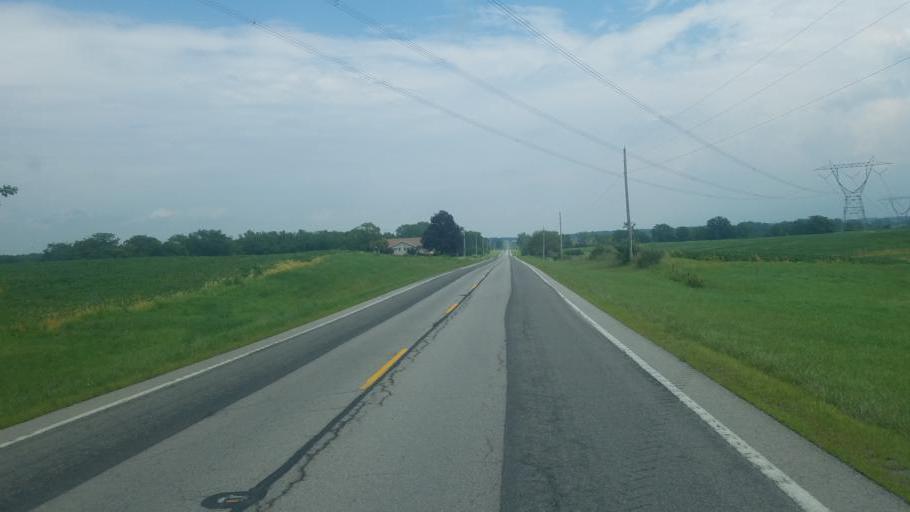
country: US
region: Ohio
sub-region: Logan County
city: Northwood
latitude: 40.4084
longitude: -83.6253
